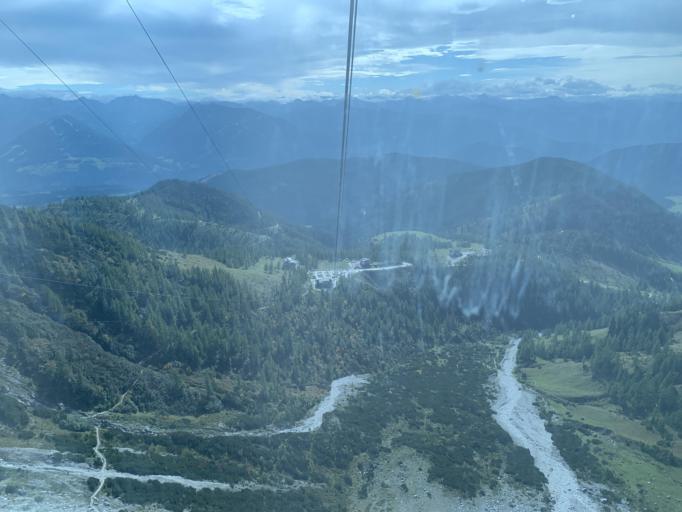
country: AT
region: Styria
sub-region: Politischer Bezirk Liezen
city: Schladming
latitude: 47.4588
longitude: 13.6217
